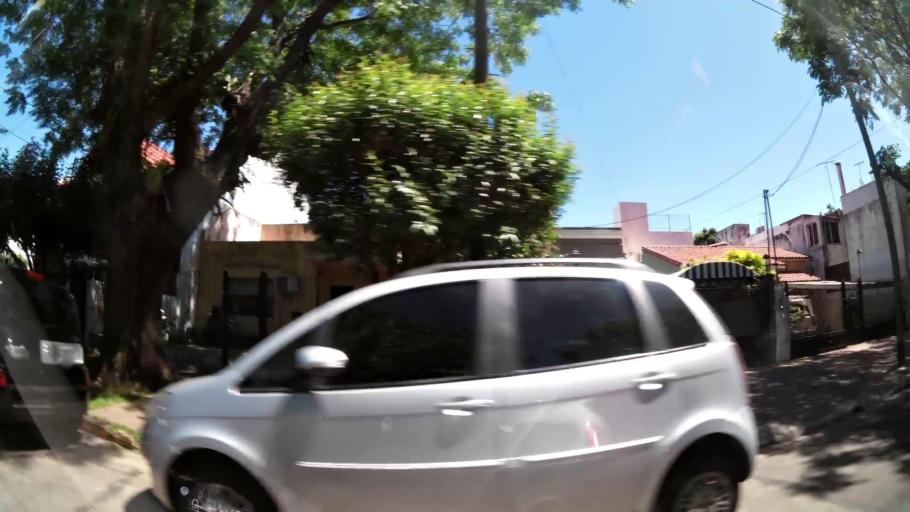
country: AR
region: Buenos Aires
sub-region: Partido de San Isidro
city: San Isidro
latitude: -34.4726
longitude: -58.5257
